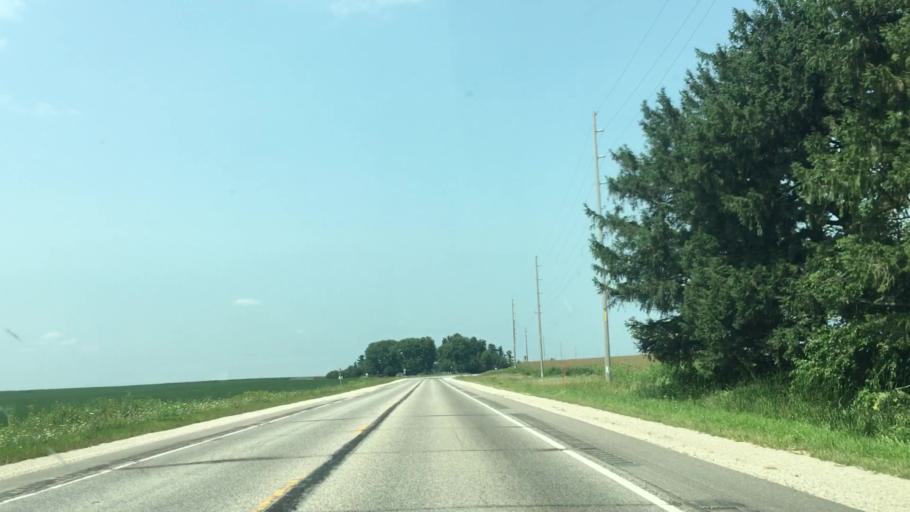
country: US
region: Iowa
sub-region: Fayette County
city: West Union
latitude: 42.9076
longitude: -91.8126
